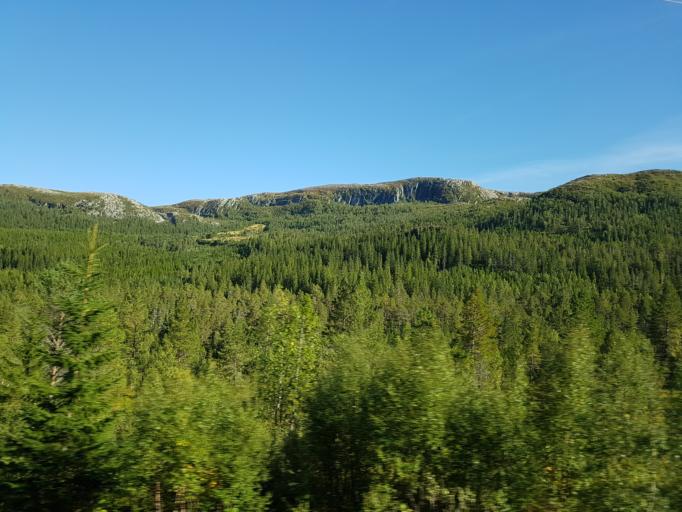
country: NO
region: Sor-Trondelag
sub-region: Afjord
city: A i Afjord
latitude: 63.7246
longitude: 10.2343
